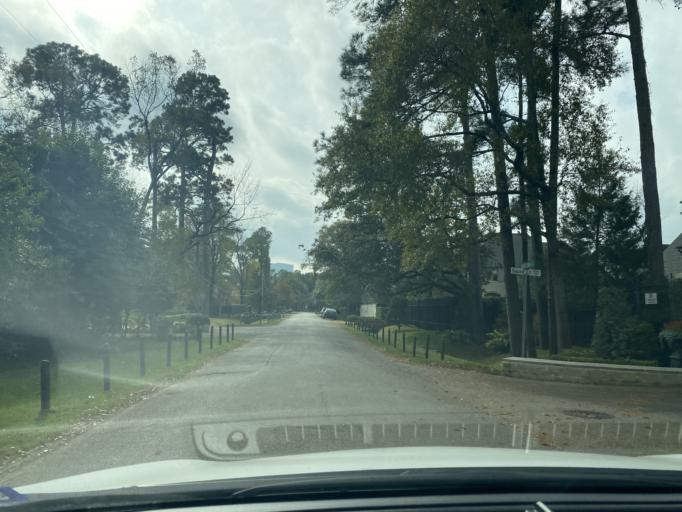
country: US
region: Texas
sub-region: Harris County
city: Hunters Creek Village
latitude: 29.7677
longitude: -95.4734
